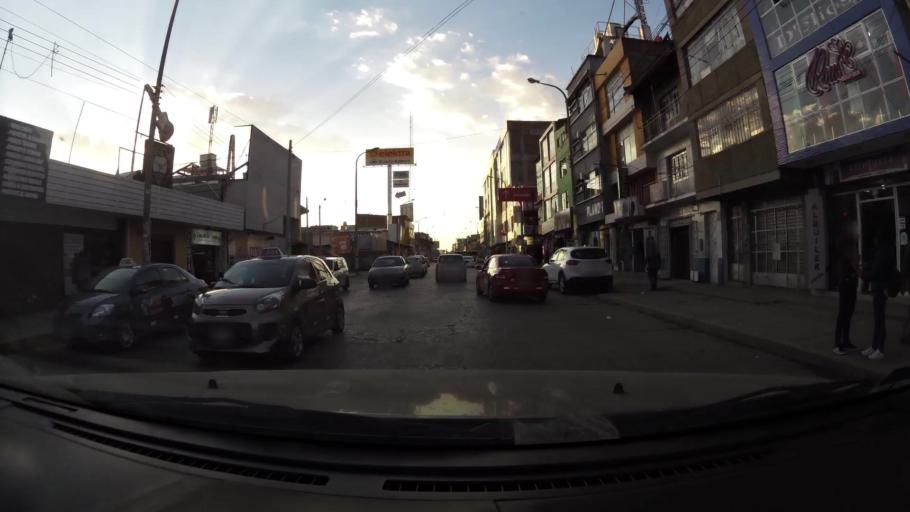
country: PE
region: Junin
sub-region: Provincia de Huancayo
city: El Tambo
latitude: -12.0627
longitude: -75.2139
